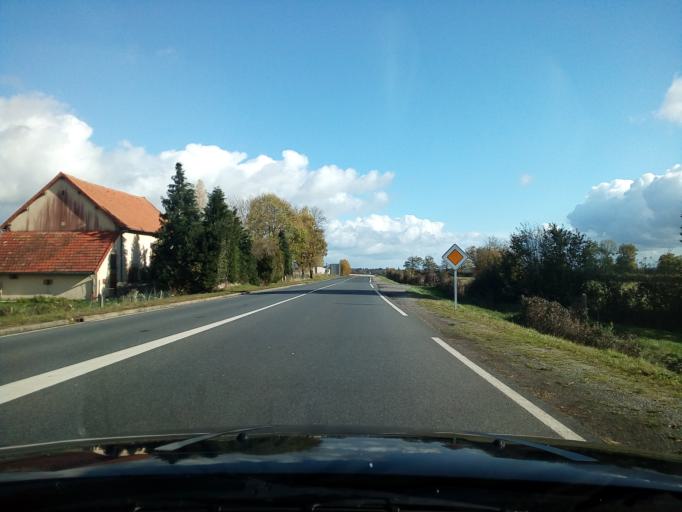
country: FR
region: Auvergne
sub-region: Departement de l'Allier
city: Montmarault
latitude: 46.3248
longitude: 2.9752
